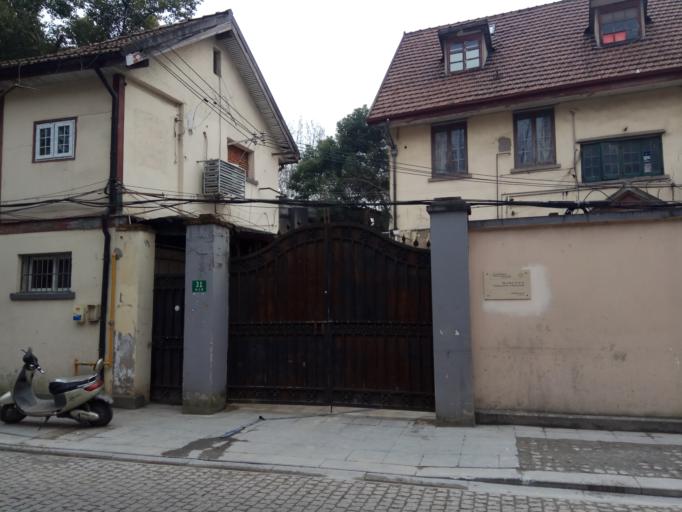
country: CN
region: Shanghai Shi
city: Xuhui
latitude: 31.2114
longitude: 121.4449
